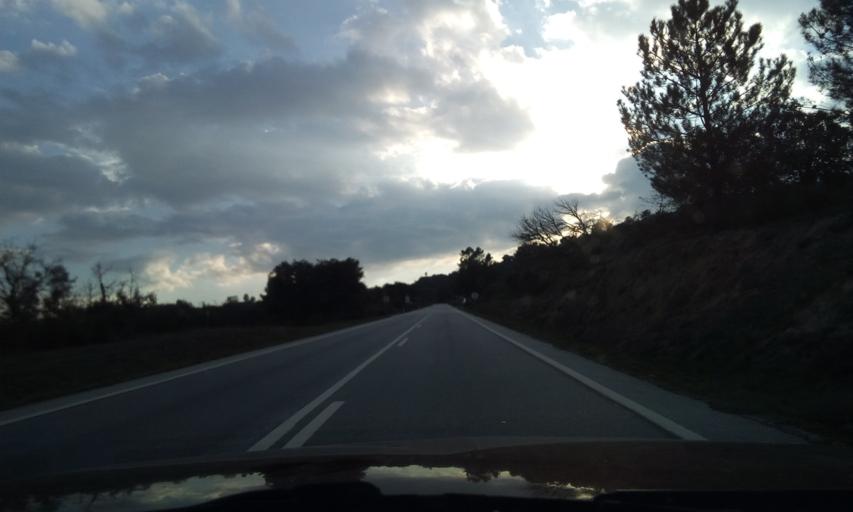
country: ES
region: Castille and Leon
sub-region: Provincia de Salamanca
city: Aldea del Obispo
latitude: 40.6936
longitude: -6.9362
